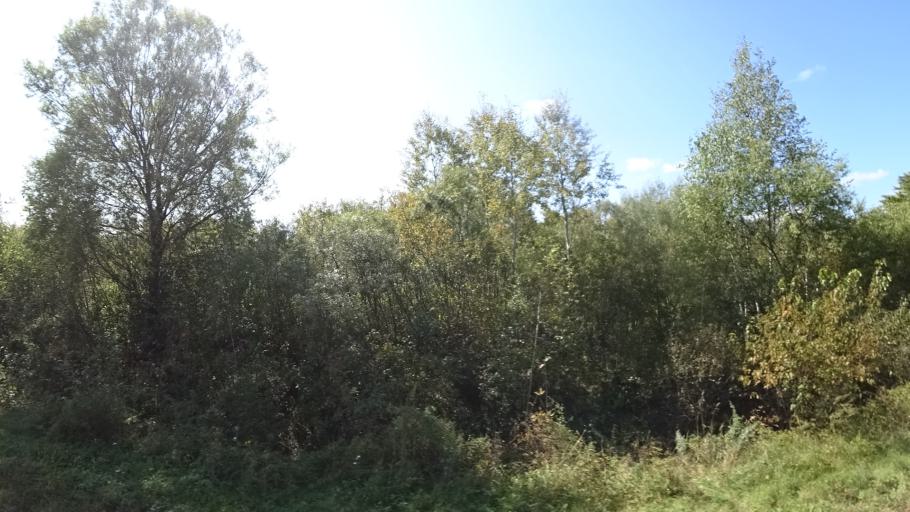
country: RU
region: Amur
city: Arkhara
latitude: 49.4022
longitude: 130.1291
